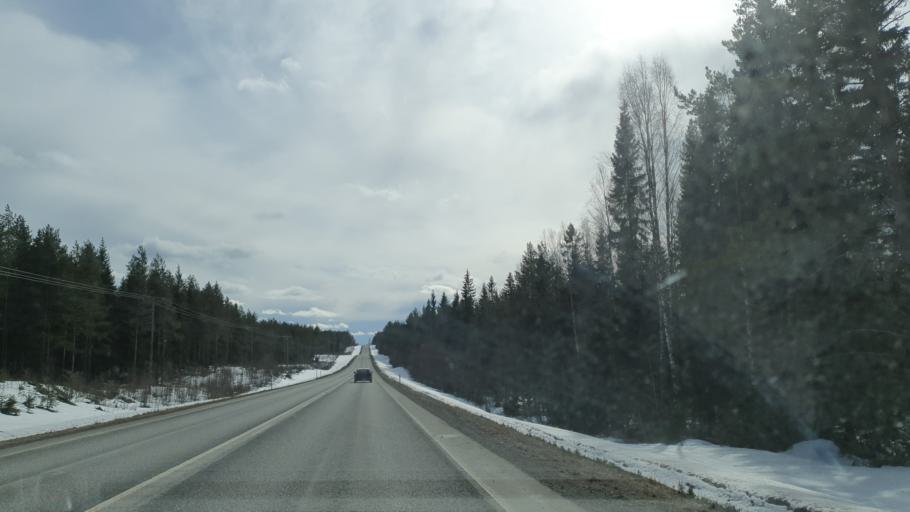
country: FI
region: Kainuu
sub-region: Kajaani
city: Ristijaervi
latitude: 64.3553
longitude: 28.0506
